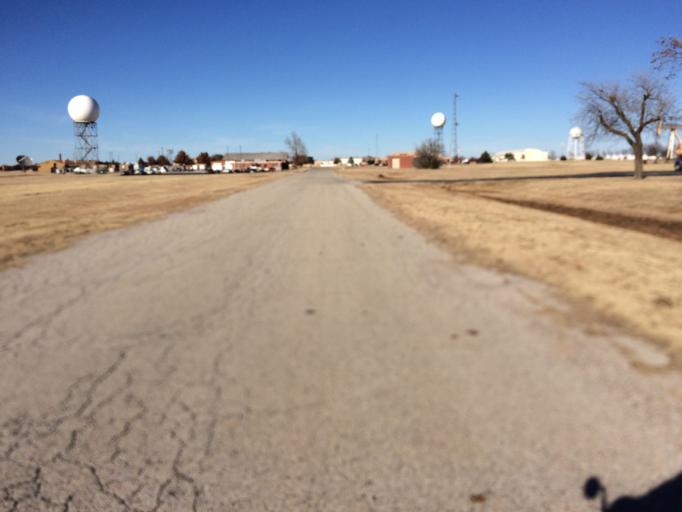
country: US
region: Oklahoma
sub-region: Cleveland County
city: Norman
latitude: 35.2338
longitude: -97.4613
